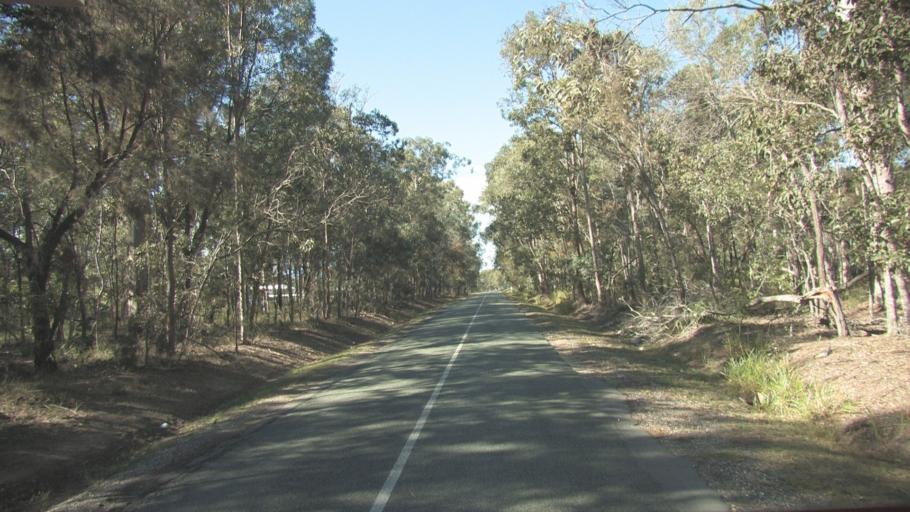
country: AU
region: Queensland
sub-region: Logan
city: Chambers Flat
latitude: -27.7929
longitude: 153.0706
